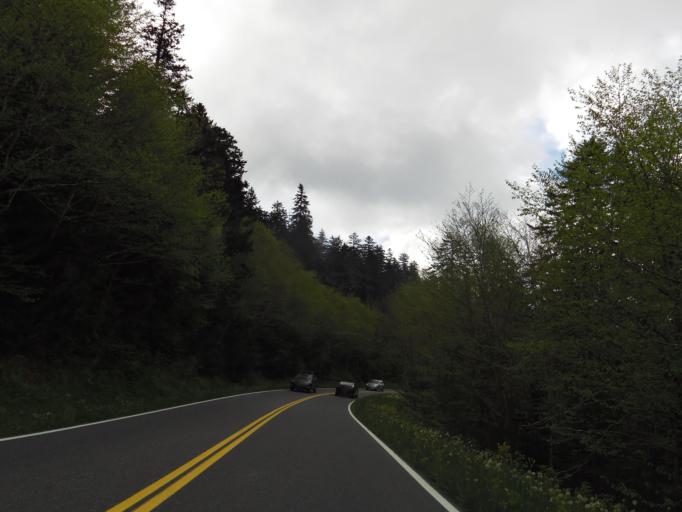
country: US
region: North Carolina
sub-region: Swain County
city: Bryson City
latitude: 35.5659
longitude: -83.4839
